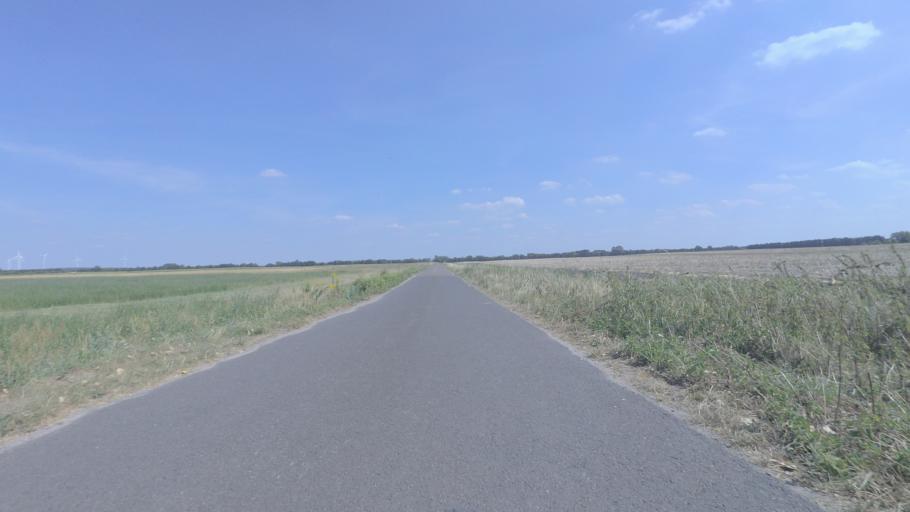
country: DE
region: Brandenburg
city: Trebbin
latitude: 52.1763
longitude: 13.2505
